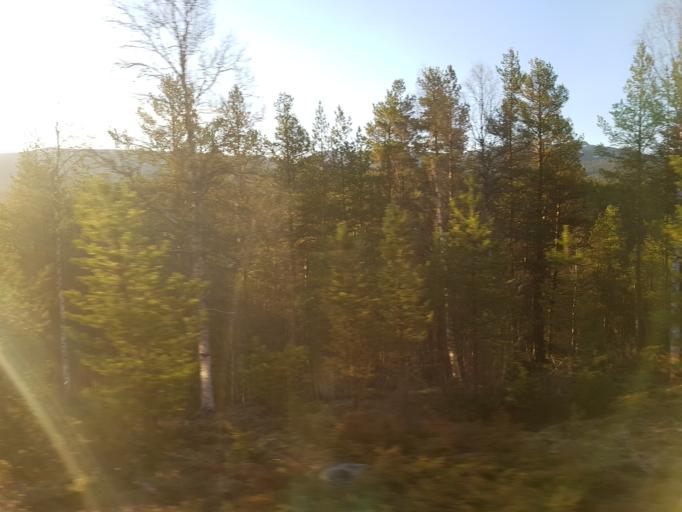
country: NO
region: Sor-Trondelag
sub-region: Oppdal
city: Oppdal
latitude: 62.6579
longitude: 9.8883
